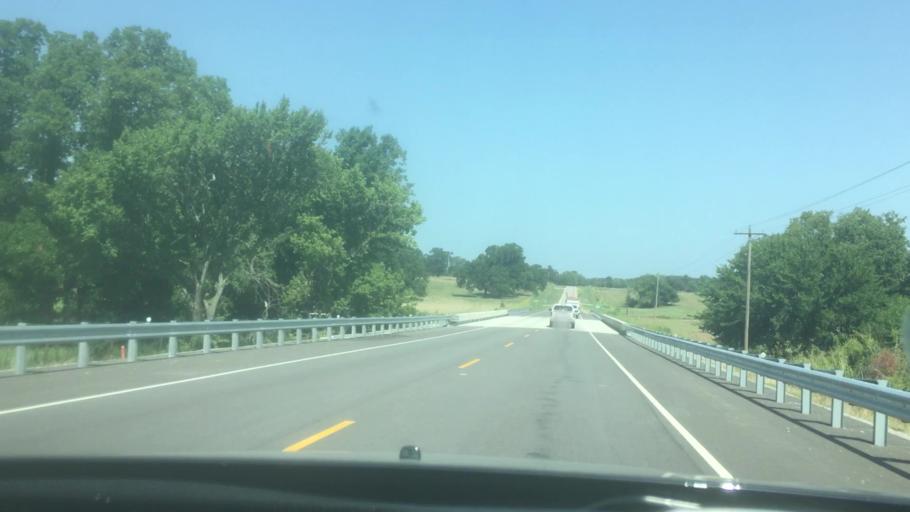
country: US
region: Oklahoma
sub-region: Bryan County
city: Durant
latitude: 34.1689
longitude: -96.4061
